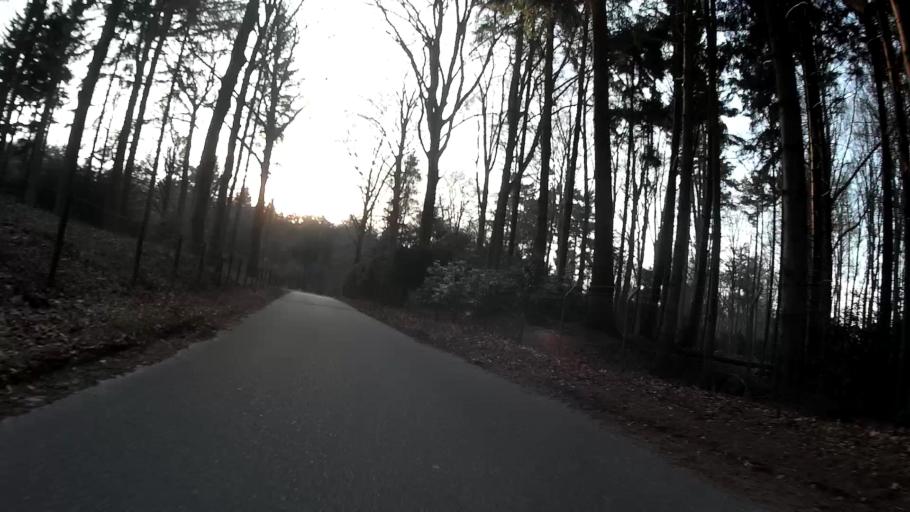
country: NL
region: Utrecht
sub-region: Gemeente Veenendaal
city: Veenendaal
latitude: 52.0081
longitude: 5.5331
